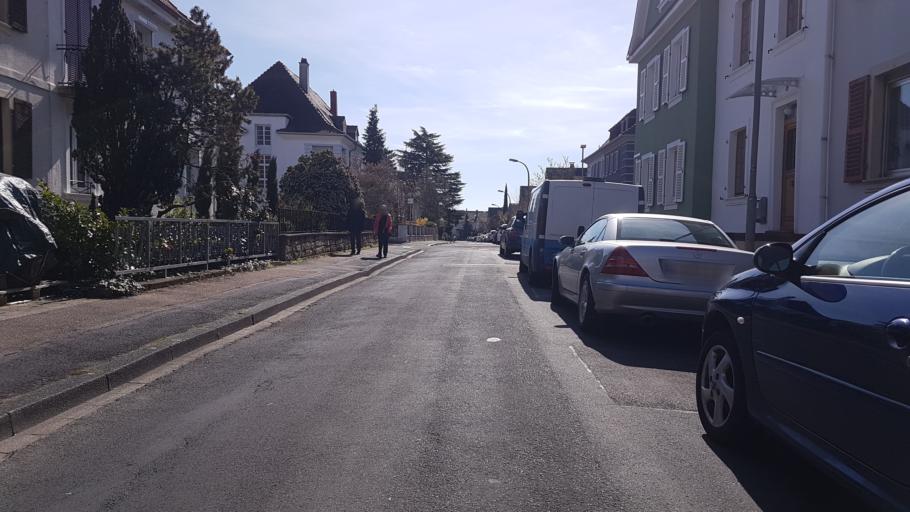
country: DE
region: Rheinland-Pfalz
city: Neustadt
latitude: 49.3450
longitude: 8.1400
